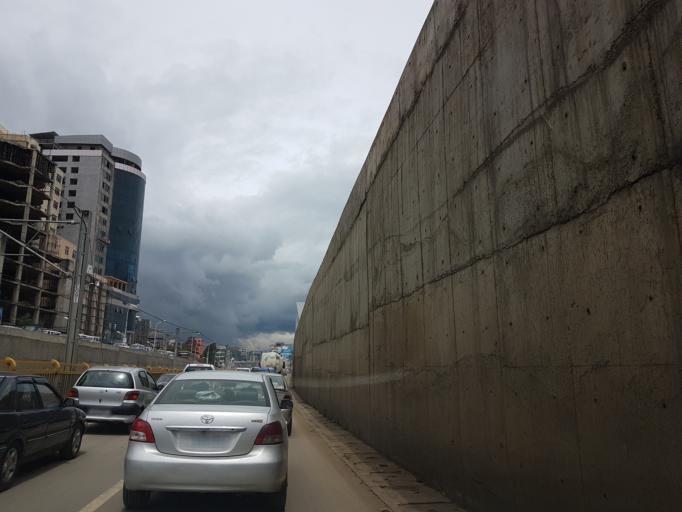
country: ET
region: Adis Abeba
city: Addis Ababa
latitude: 9.0187
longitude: 38.8004
